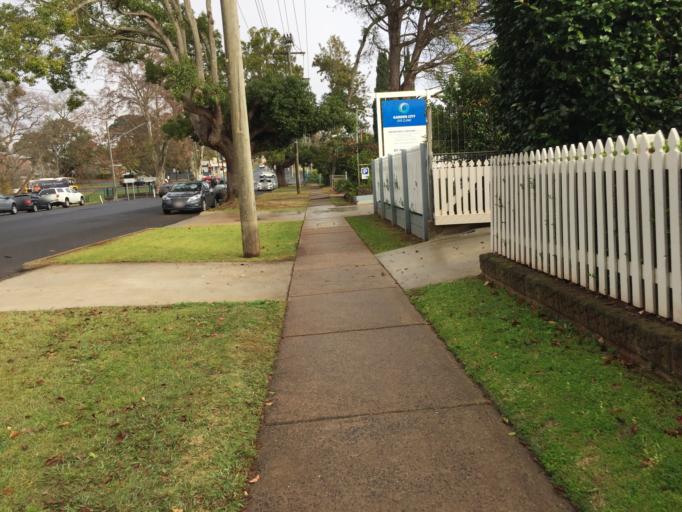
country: AU
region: Queensland
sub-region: Toowoomba
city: Toowoomba
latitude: -27.5661
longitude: 151.9629
